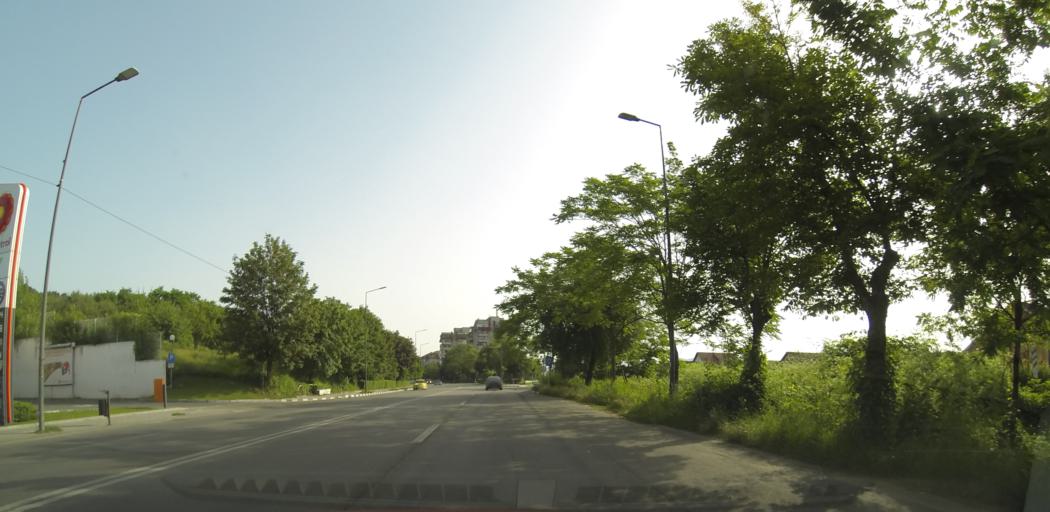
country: RO
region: Valcea
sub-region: Municipiul Ramnicu Valcea
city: Ramnicu Valcea
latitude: 45.0883
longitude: 24.3599
